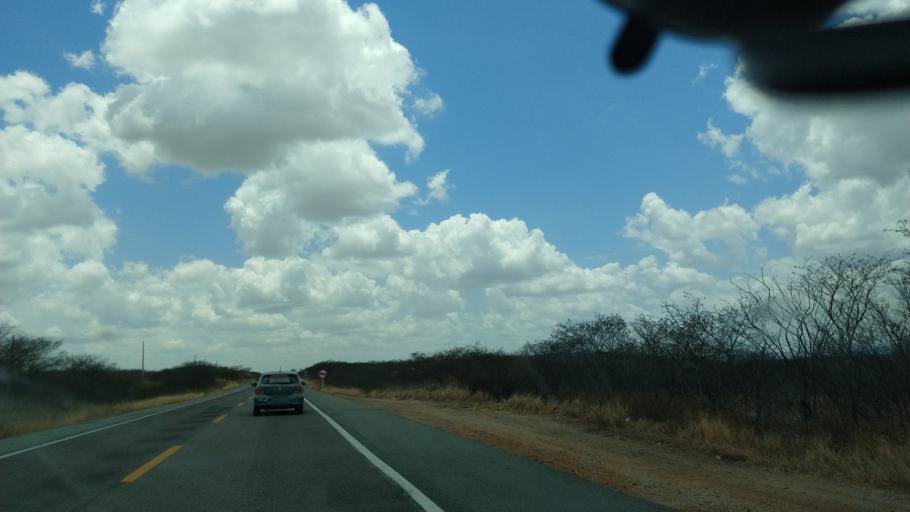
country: BR
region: Rio Grande do Norte
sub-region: Cerro Cora
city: Cerro Cora
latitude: -6.2080
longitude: -36.2870
